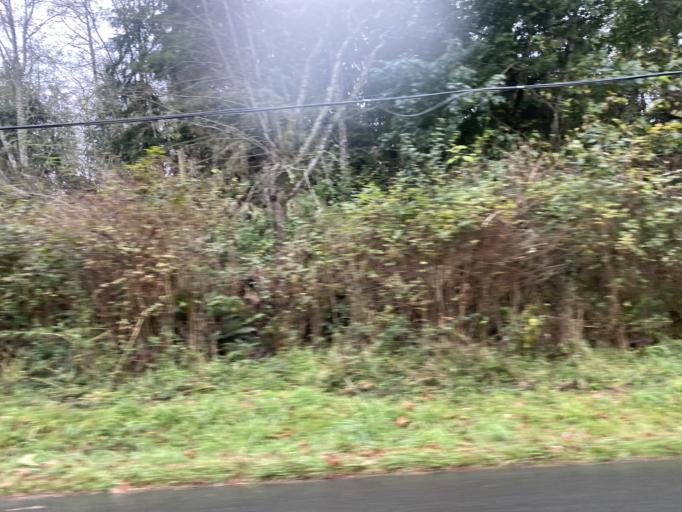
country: US
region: Washington
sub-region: Island County
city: Freeland
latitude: 48.0921
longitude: -122.4910
